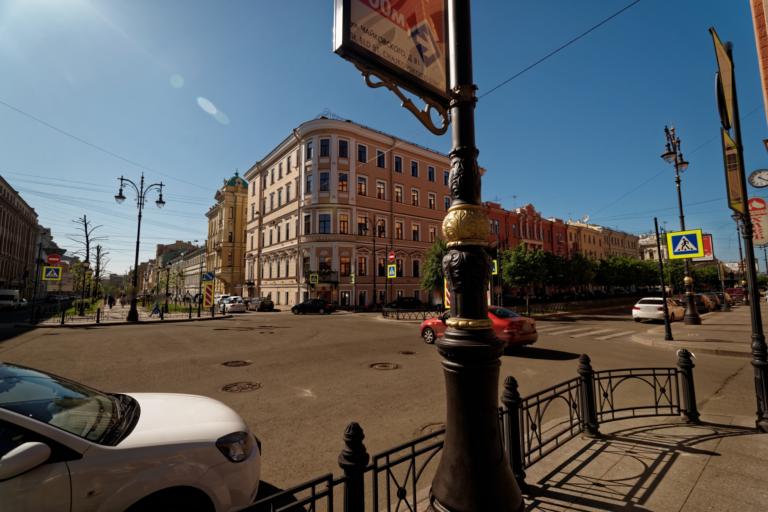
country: RU
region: St.-Petersburg
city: Centralniy
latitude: 59.9451
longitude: 30.3595
